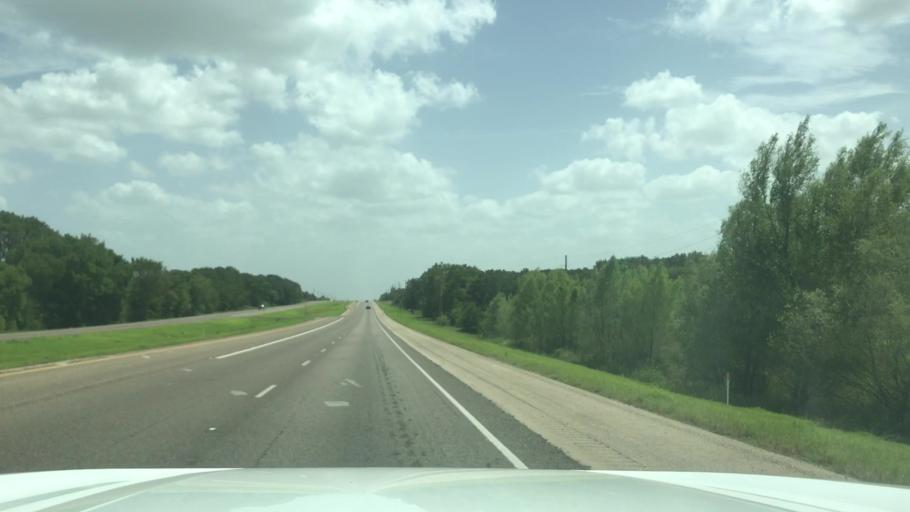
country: US
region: Texas
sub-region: Robertson County
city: Calvert
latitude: 31.0898
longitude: -96.7145
